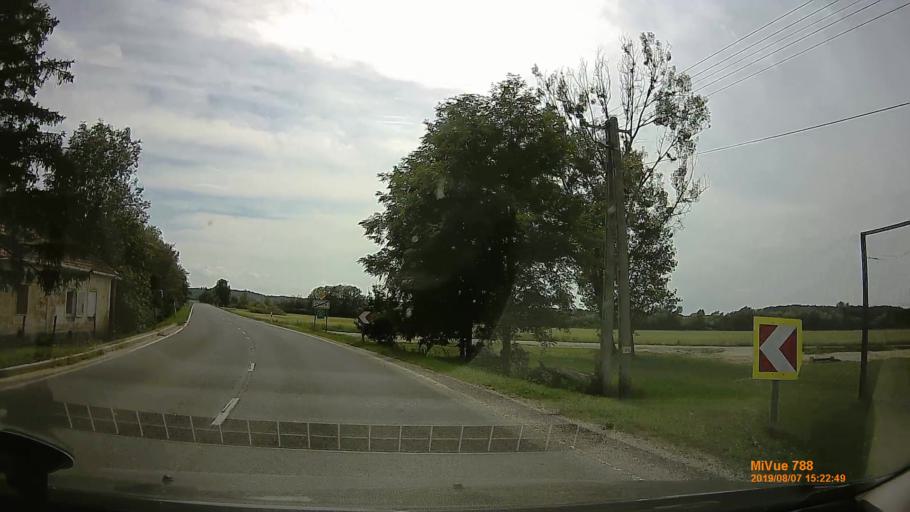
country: HU
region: Vas
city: Sarvar
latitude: 47.3257
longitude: 16.8498
